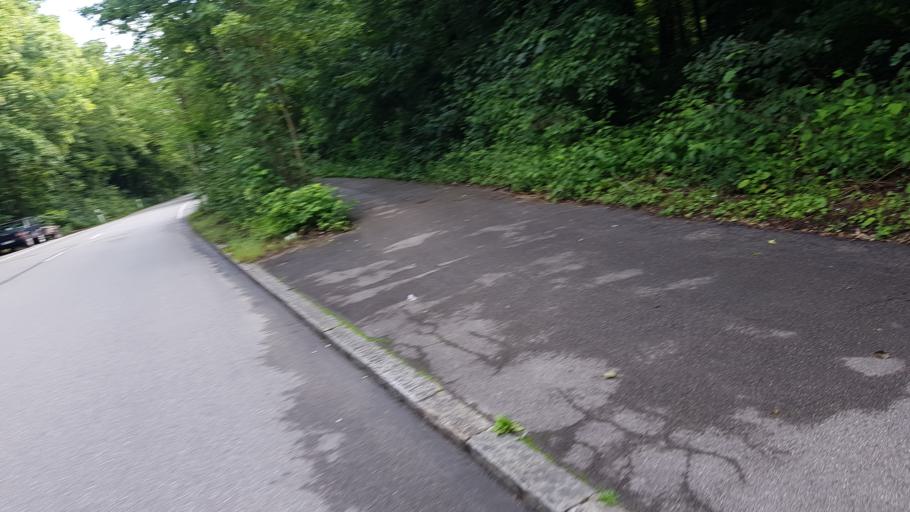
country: DE
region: Bavaria
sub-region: Upper Bavaria
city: Pasing
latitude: 48.1663
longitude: 11.4926
